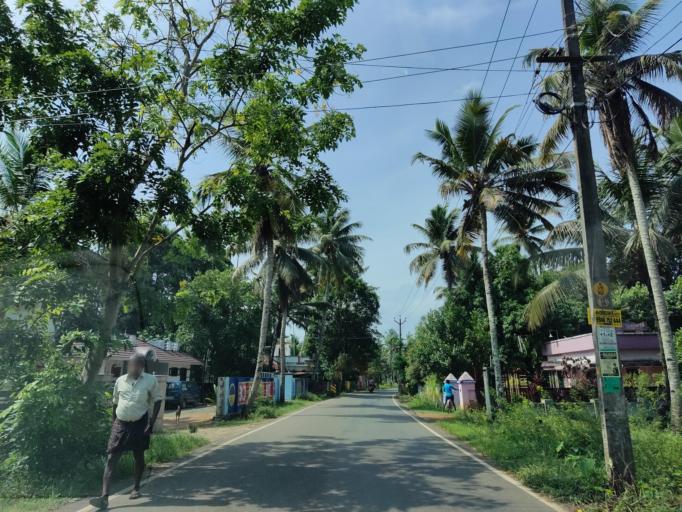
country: IN
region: Kerala
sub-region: Alappuzha
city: Mavelikara
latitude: 9.3316
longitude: 76.4675
